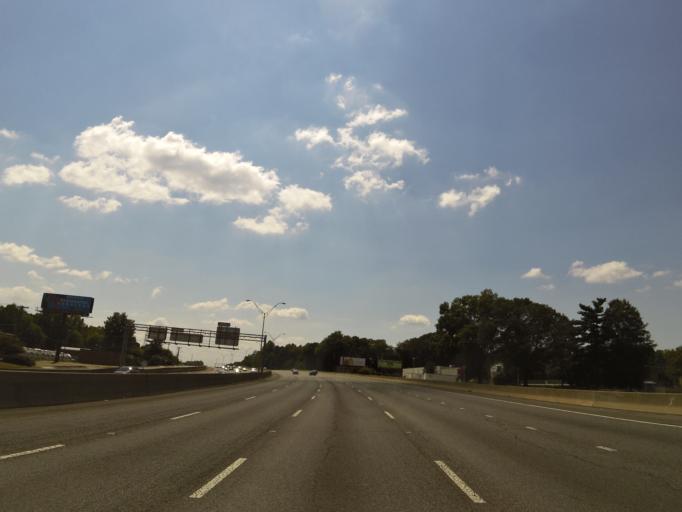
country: US
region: North Carolina
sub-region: Mecklenburg County
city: Charlotte
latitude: 35.2677
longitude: -80.8717
